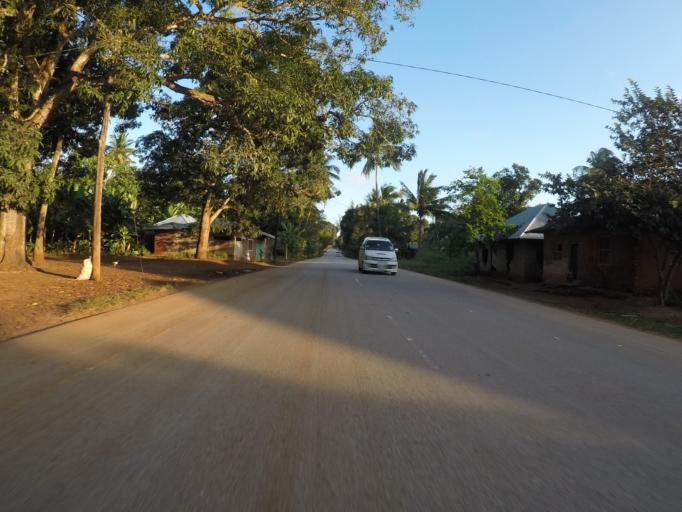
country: TZ
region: Zanzibar North
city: Mkokotoni
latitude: -5.8719
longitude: 39.2811
